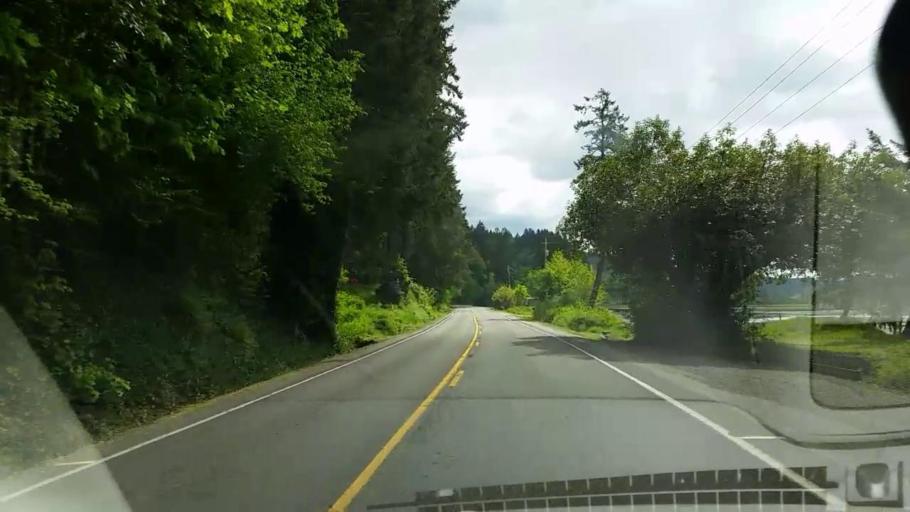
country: US
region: Washington
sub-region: Mason County
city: Shelton
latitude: 47.3431
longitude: -123.1093
